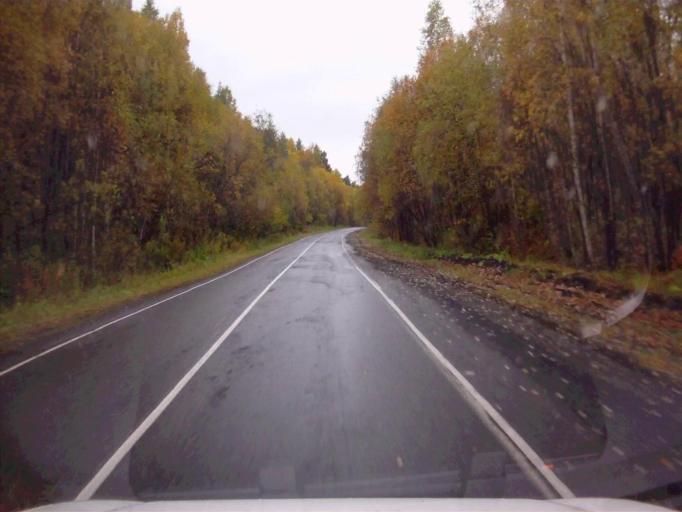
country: RU
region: Chelyabinsk
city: Verkhniy Ufaley
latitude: 56.0446
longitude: 60.1100
